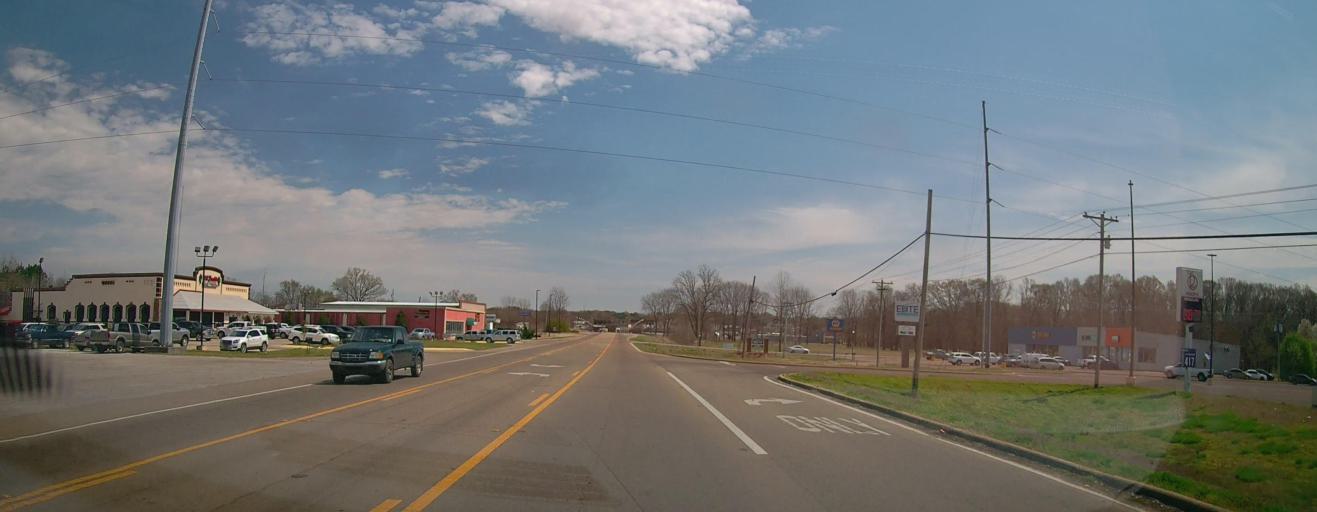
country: US
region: Mississippi
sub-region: Union County
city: New Albany
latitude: 34.4957
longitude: -89.0172
